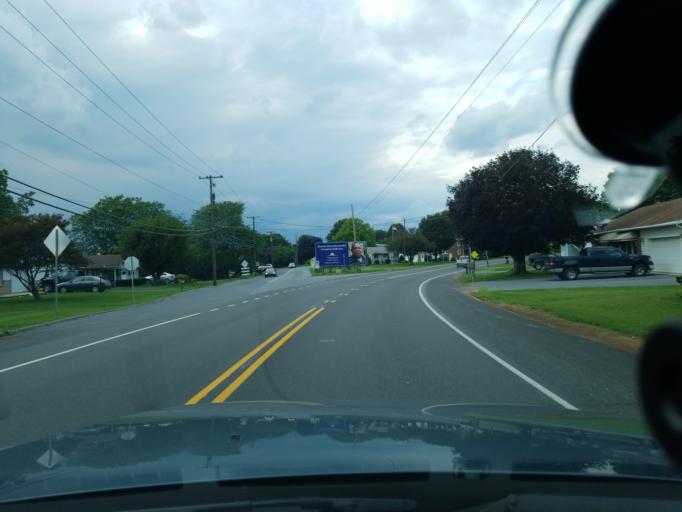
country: US
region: Pennsylvania
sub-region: Lebanon County
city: Myerstown
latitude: 40.3814
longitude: -76.3070
